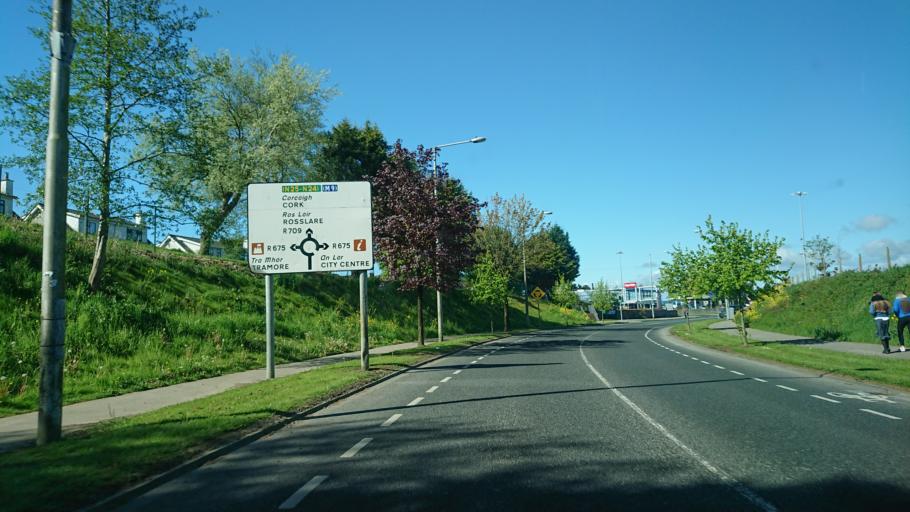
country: IE
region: Munster
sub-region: Waterford
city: Waterford
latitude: 52.2473
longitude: -7.1174
